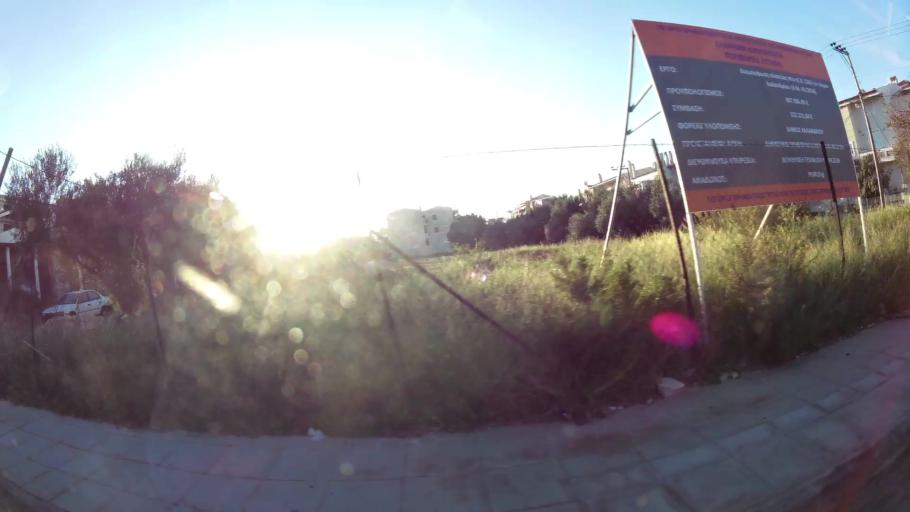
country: GR
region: Attica
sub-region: Nomarchia Anatolikis Attikis
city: Gerakas
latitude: 38.0323
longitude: 23.8467
